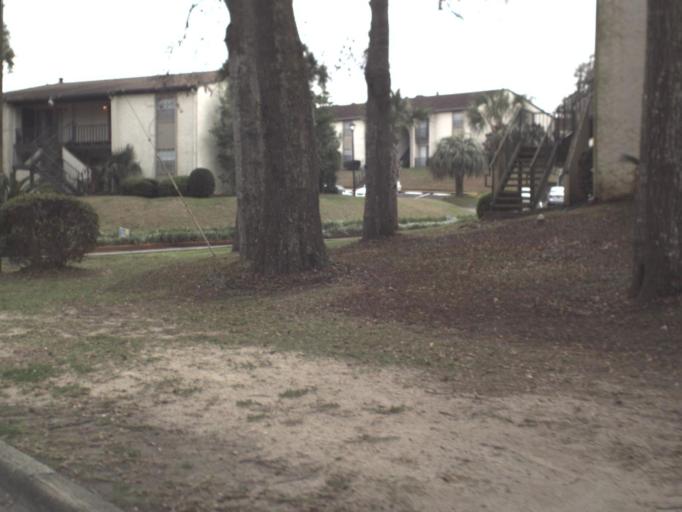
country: US
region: Florida
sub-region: Leon County
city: Tallahassee
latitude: 30.4705
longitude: -84.2773
